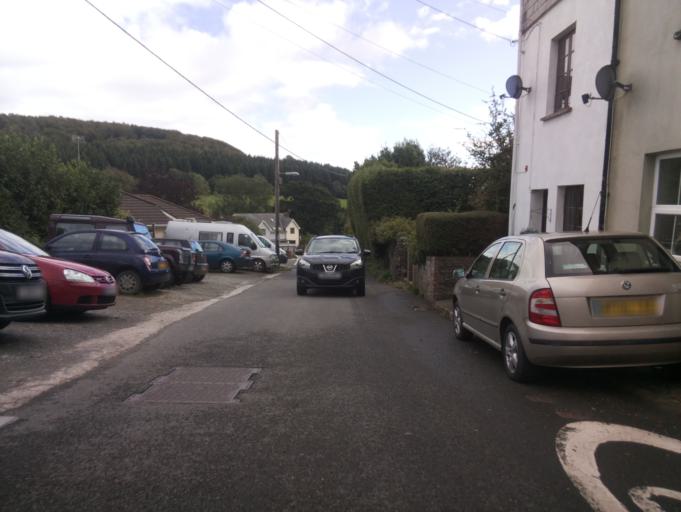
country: GB
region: England
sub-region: Devon
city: Ivybridge
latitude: 50.3610
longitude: -3.9171
